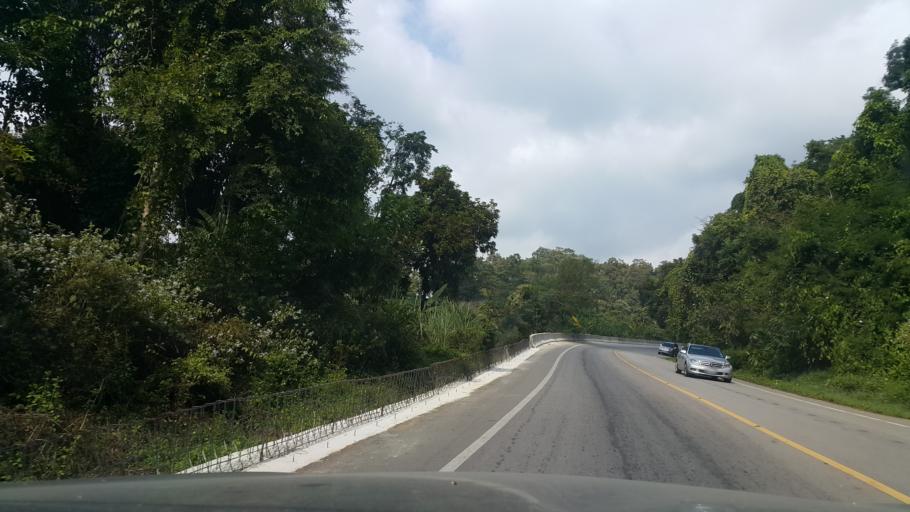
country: TH
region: Lampang
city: Wang Nuea
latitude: 19.0646
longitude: 99.7312
